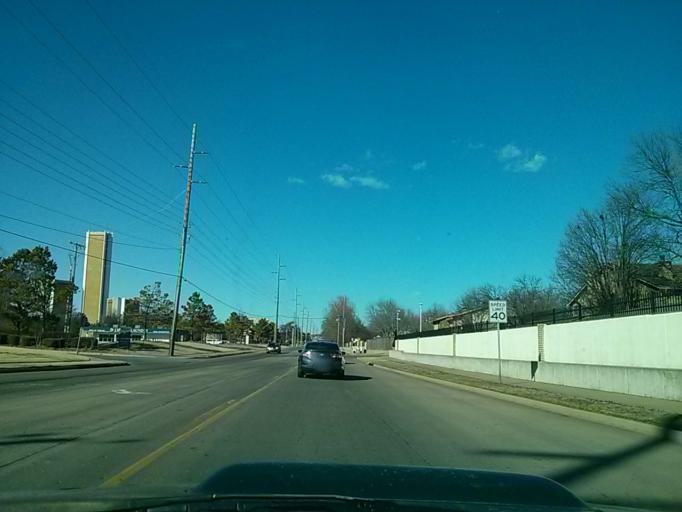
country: US
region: Oklahoma
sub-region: Tulsa County
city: Jenks
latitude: 36.0328
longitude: -95.9489
